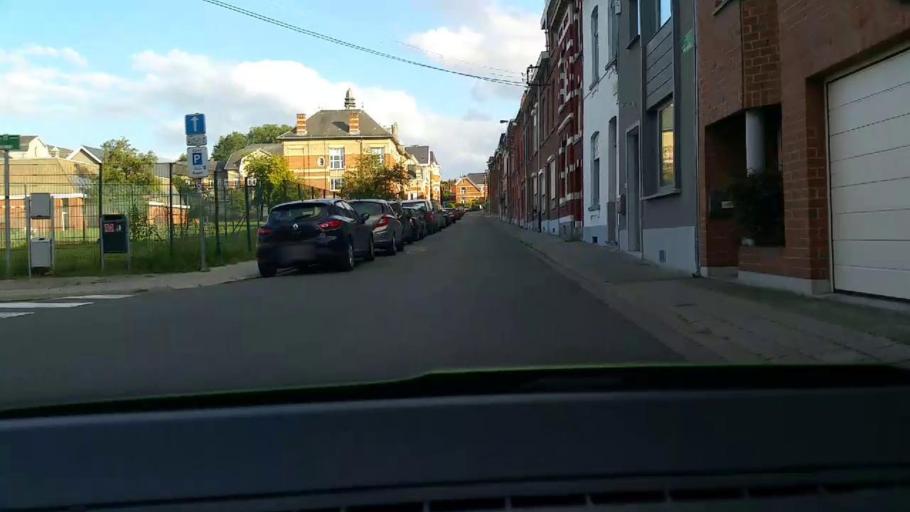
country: BE
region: Wallonia
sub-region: Province du Brabant Wallon
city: Nivelles
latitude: 50.5973
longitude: 4.3299
